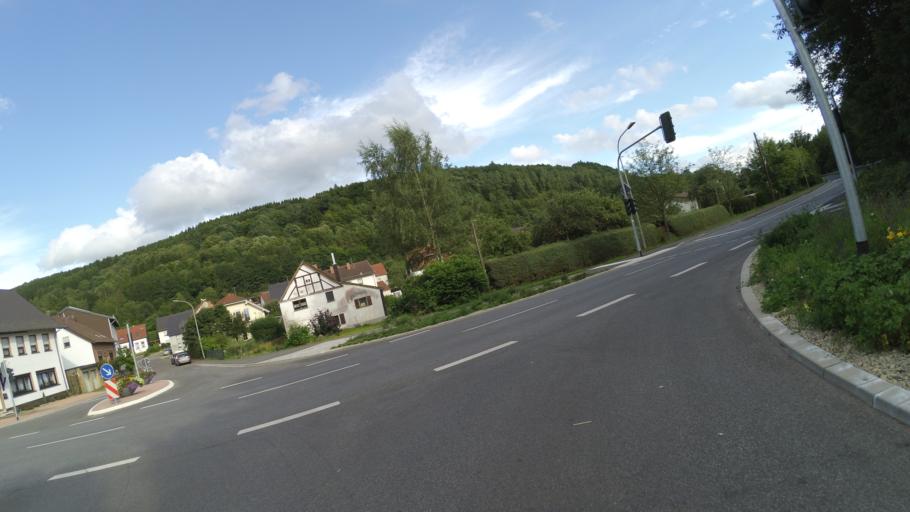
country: DE
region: Saarland
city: Nonnweiler
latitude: 49.5693
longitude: 6.9697
